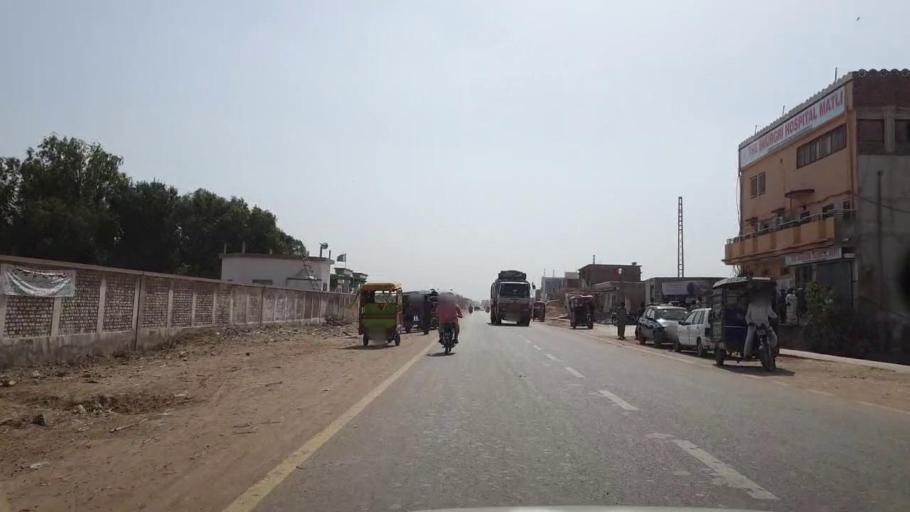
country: PK
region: Sindh
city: Matli
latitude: 25.0524
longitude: 68.6466
